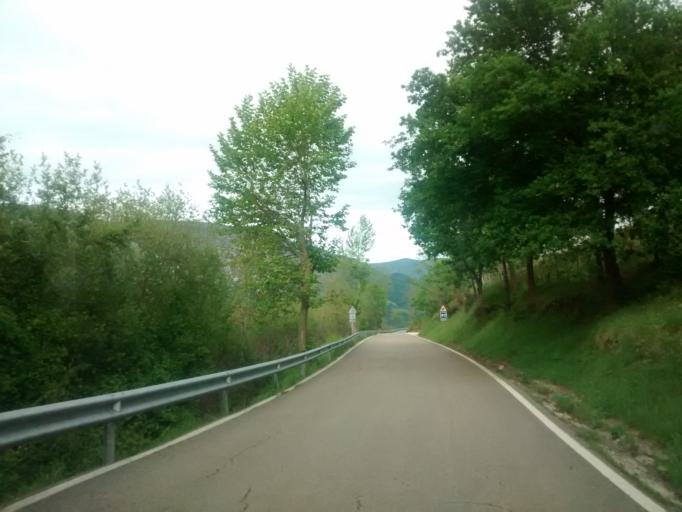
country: ES
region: Cantabria
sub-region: Provincia de Cantabria
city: San Vicente de la Barquera
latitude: 43.2536
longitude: -4.4372
